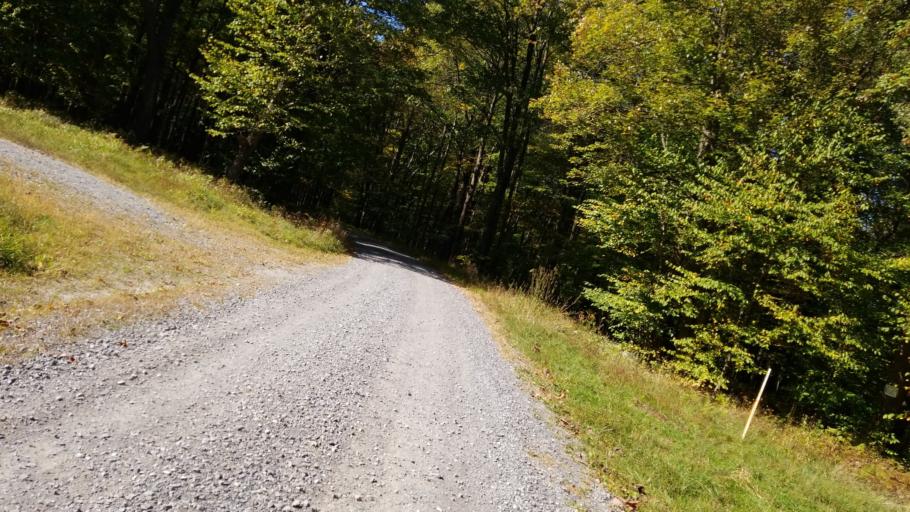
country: US
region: Pennsylvania
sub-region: Clearfield County
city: Clearfield
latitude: 41.1839
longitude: -78.5000
